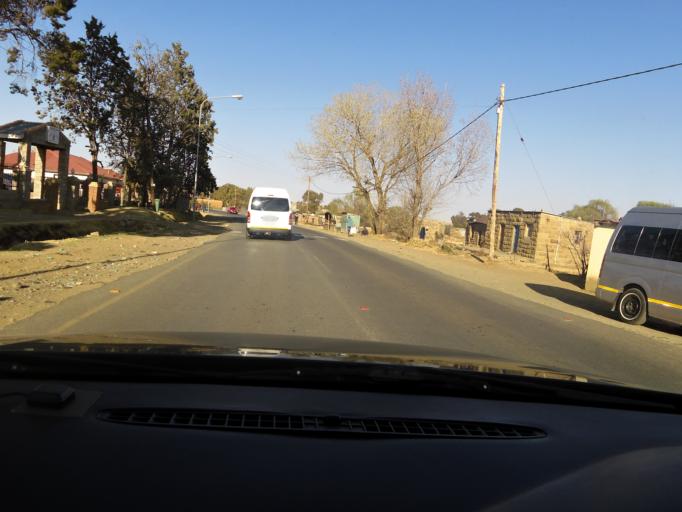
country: LS
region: Mafeteng
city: Mafeteng
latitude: -29.8234
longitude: 27.2373
